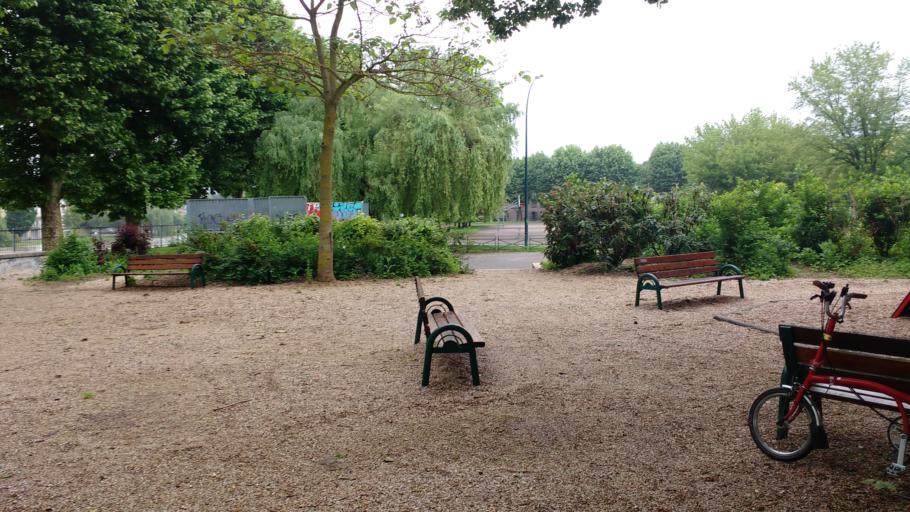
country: FR
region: Bourgogne
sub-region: Departement de l'Yonne
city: Sens
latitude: 48.1992
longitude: 3.2770
